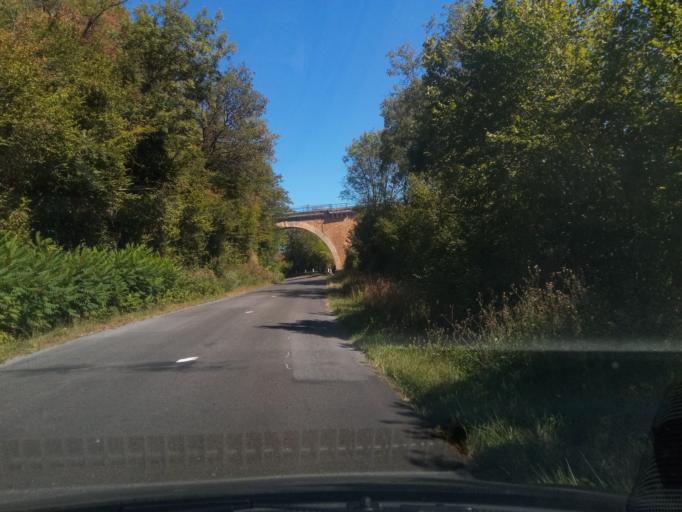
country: FR
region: Poitou-Charentes
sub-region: Departement de la Vienne
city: Saulge
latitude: 46.4060
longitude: 0.8778
